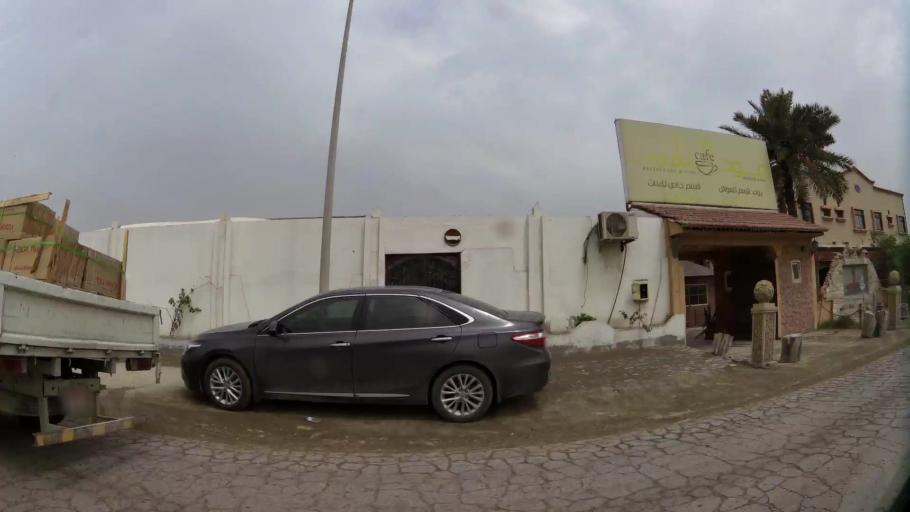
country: BH
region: Northern
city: Ar Rifa'
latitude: 26.1323
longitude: 50.5908
